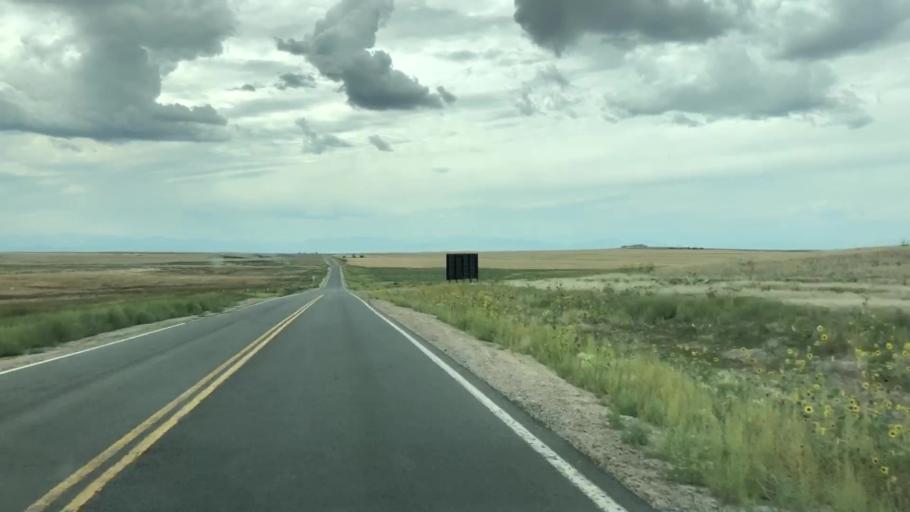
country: US
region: Colorado
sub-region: Adams County
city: Aurora
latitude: 39.7985
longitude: -104.6885
